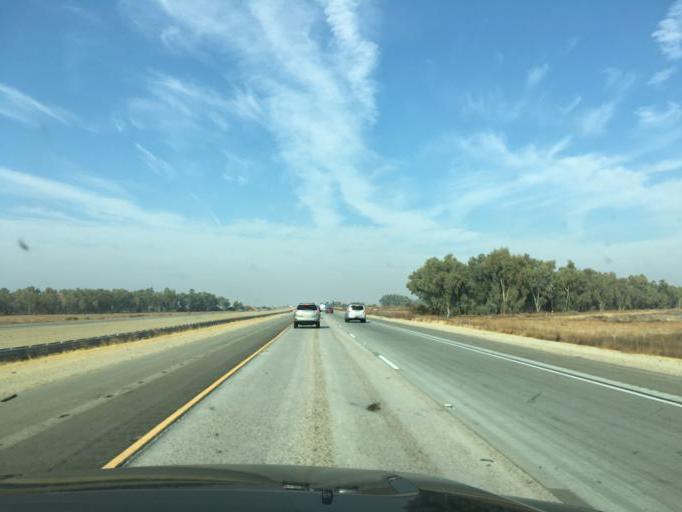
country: US
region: California
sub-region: Kern County
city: Lost Hills
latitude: 35.5933
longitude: -119.6333
